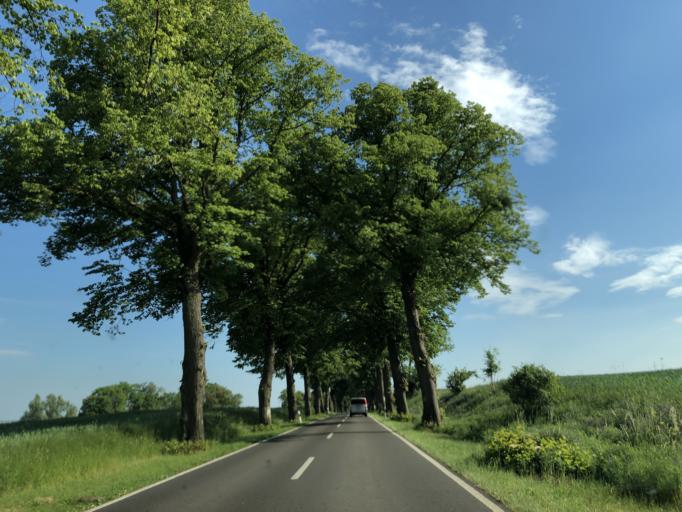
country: DE
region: Brandenburg
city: Zichow
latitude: 53.1187
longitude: 13.9621
